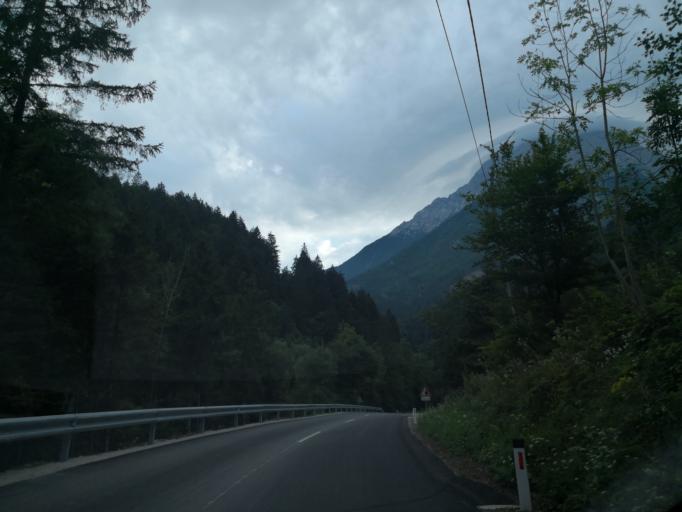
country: SI
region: Jezersko
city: Zgornje Jezersko
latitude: 46.3266
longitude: 14.4934
